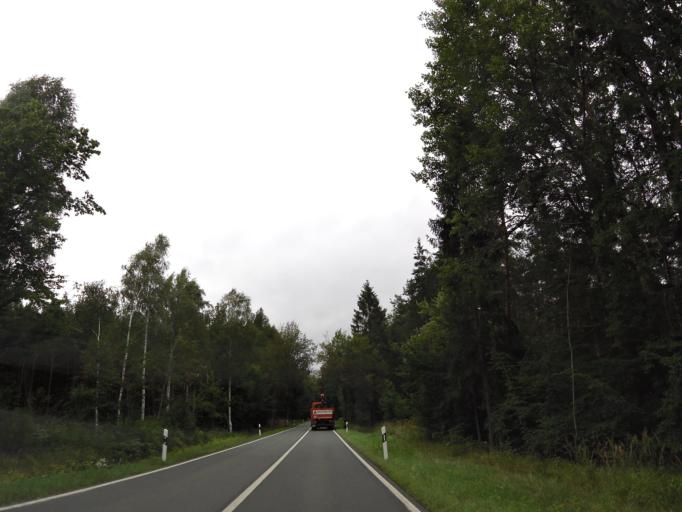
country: DE
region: Thuringia
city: Hainspitz
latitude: 50.9370
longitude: 11.8513
